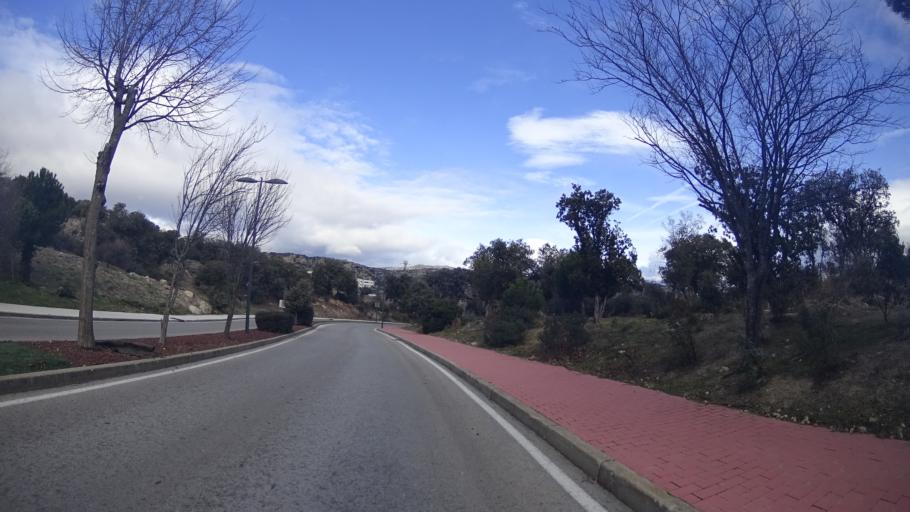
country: ES
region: Madrid
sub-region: Provincia de Madrid
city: Torrelodones
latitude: 40.5754
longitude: -3.9363
